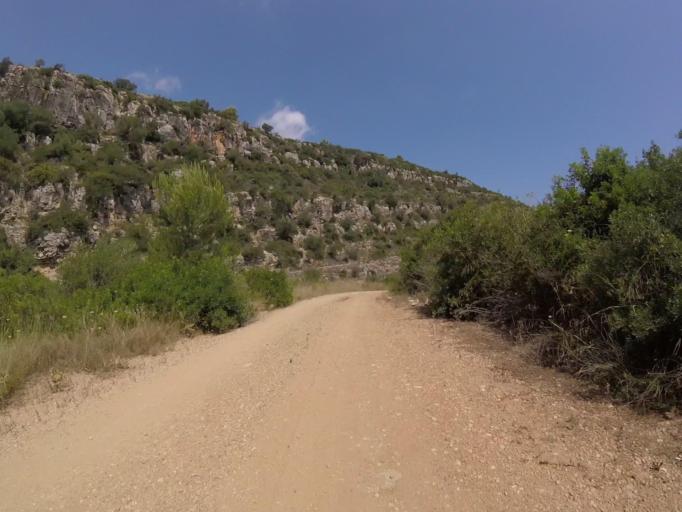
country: ES
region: Valencia
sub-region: Provincia de Castello
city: Torreblanca
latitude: 40.2212
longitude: 0.1472
